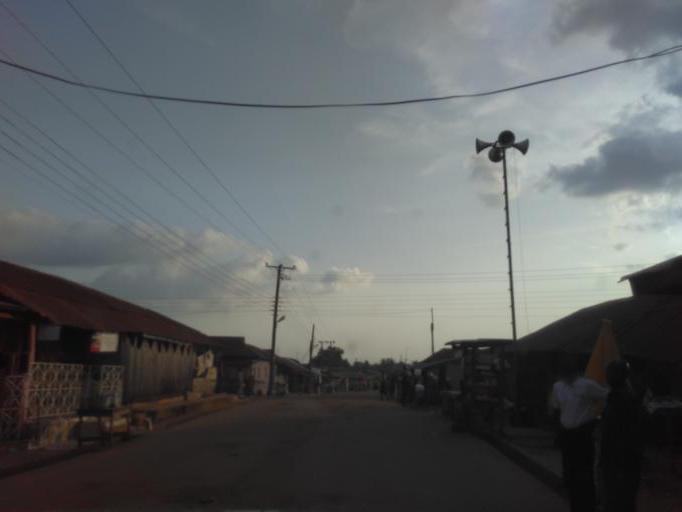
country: GH
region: Ashanti
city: Mamponteng
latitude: 6.6863
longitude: -1.4386
